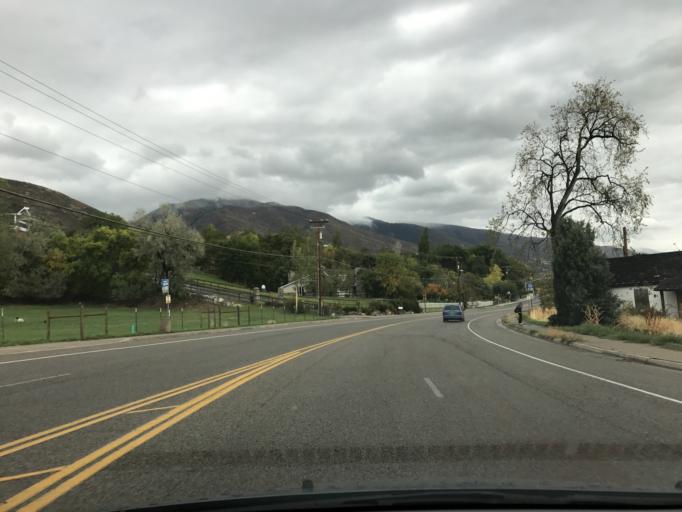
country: US
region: Utah
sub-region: Davis County
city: Fruit Heights
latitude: 41.0101
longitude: -111.9096
